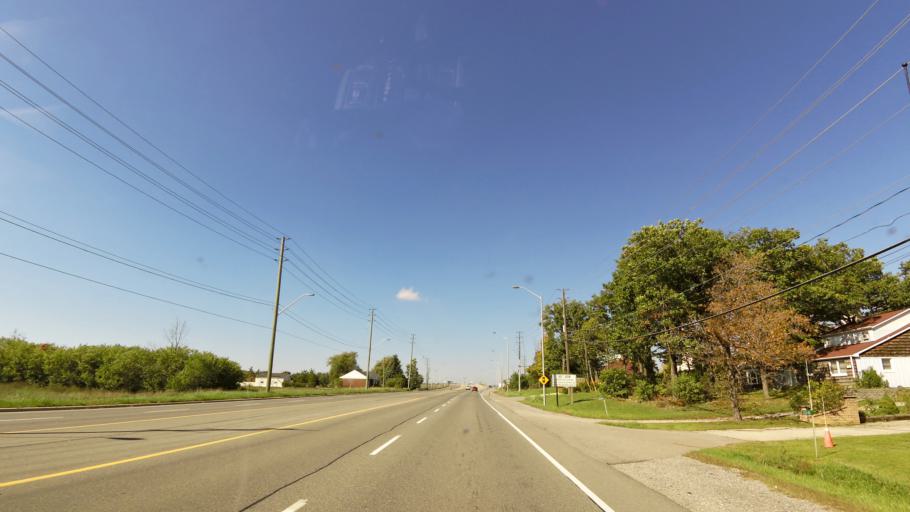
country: CA
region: Ontario
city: Burlington
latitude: 43.4415
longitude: -79.7845
